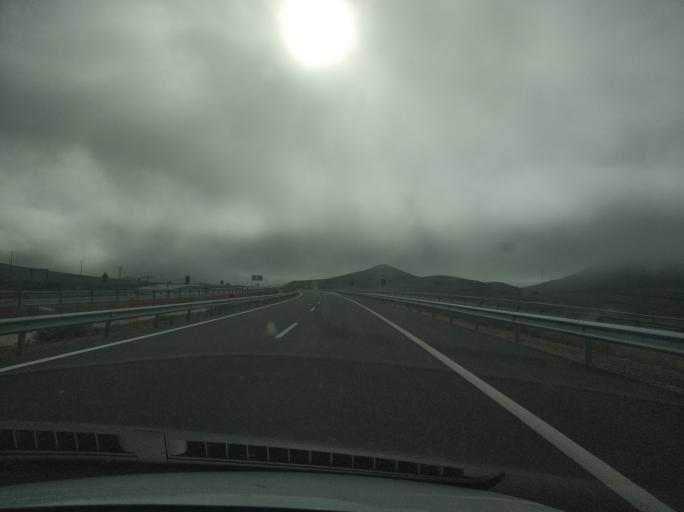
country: ES
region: Castille and Leon
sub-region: Provincia de Soria
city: Yelo
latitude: 41.2174
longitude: -2.4715
